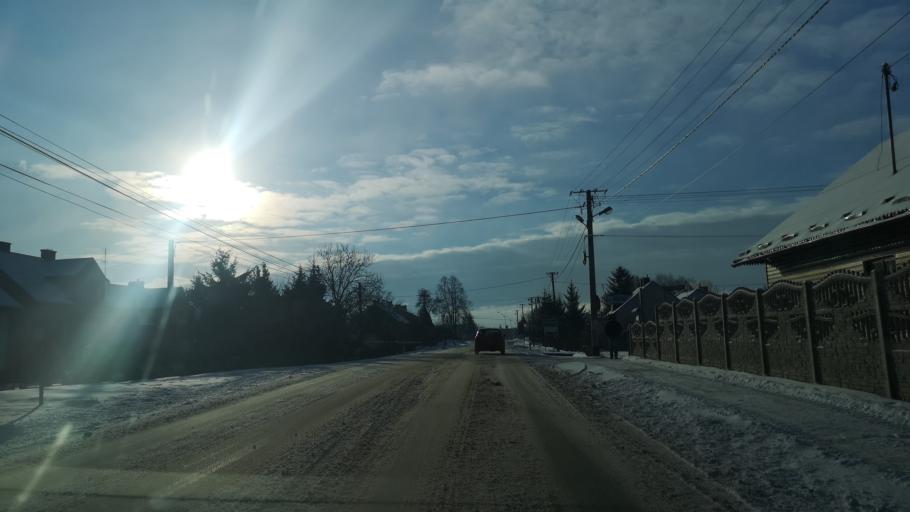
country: PL
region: Subcarpathian Voivodeship
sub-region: Powiat przeworski
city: Gorliczyna
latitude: 50.0870
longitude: 22.4923
